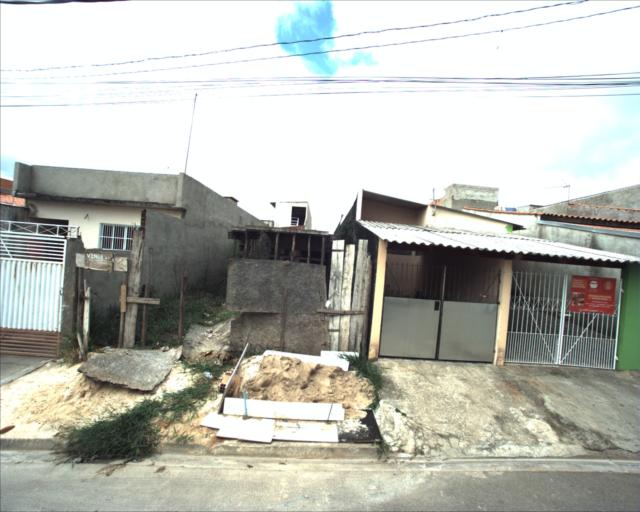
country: BR
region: Sao Paulo
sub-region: Sorocaba
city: Sorocaba
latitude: -23.4359
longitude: -47.4974
